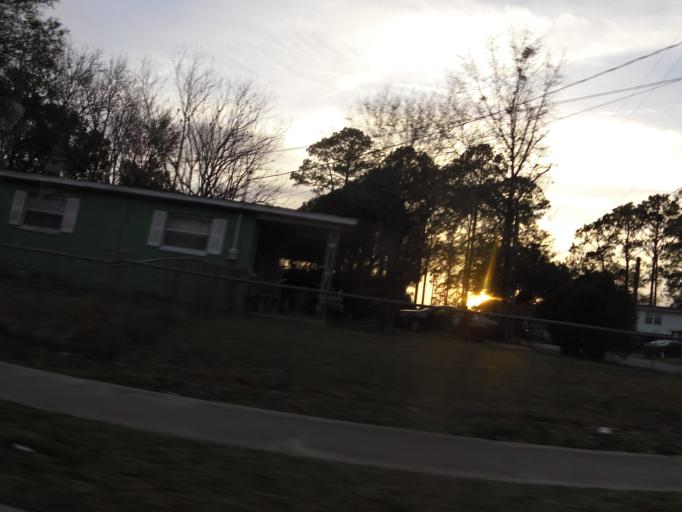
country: US
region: Florida
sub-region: Duval County
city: Jacksonville
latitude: 30.3686
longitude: -81.7091
